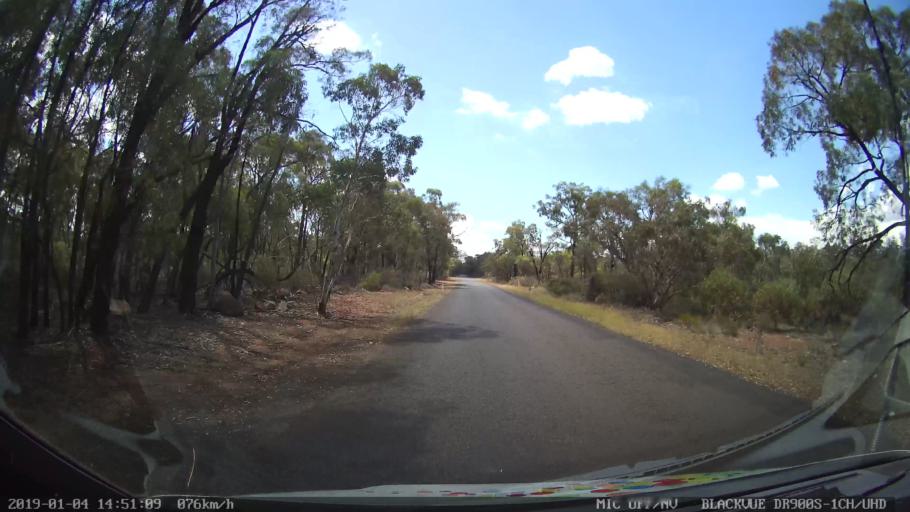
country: AU
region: New South Wales
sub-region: Dubbo Municipality
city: Dubbo
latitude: -32.0302
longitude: 148.6538
